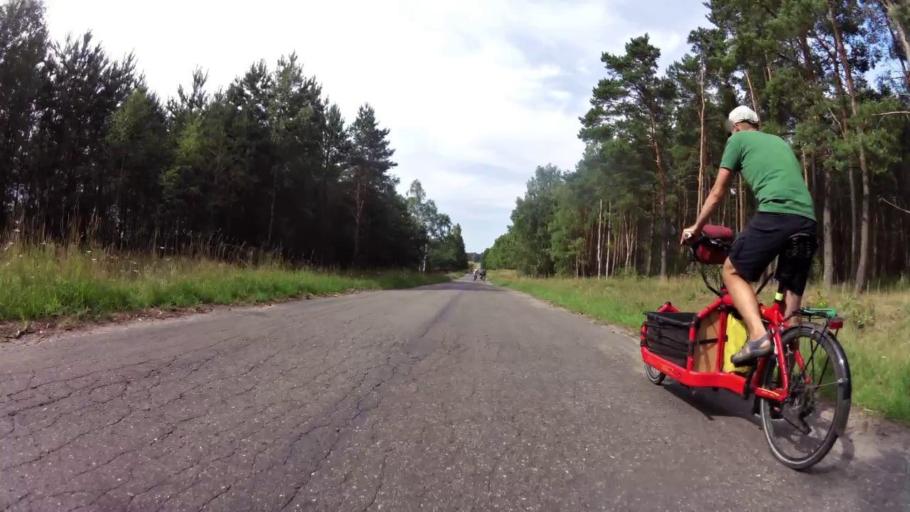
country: PL
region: West Pomeranian Voivodeship
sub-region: Powiat stargardzki
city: Insko
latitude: 53.4042
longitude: 15.6013
